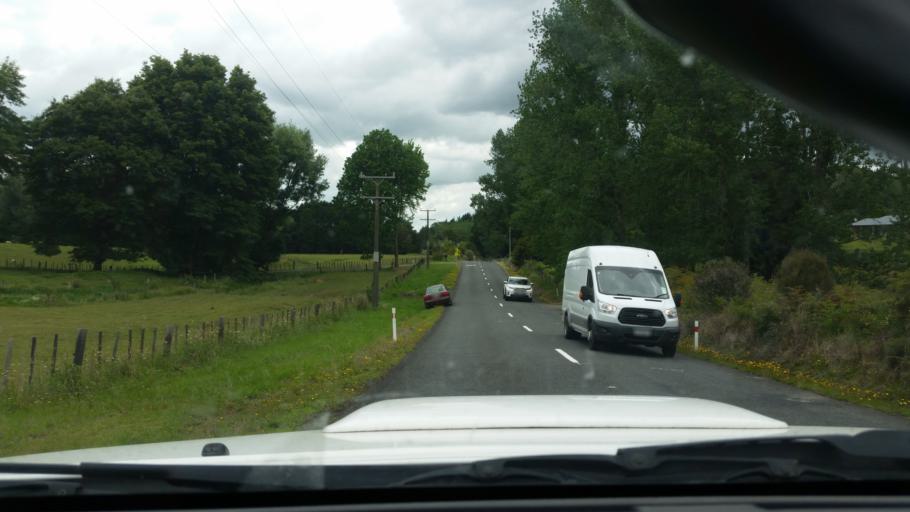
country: NZ
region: Northland
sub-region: Kaipara District
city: Dargaville
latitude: -35.7437
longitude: 173.8769
